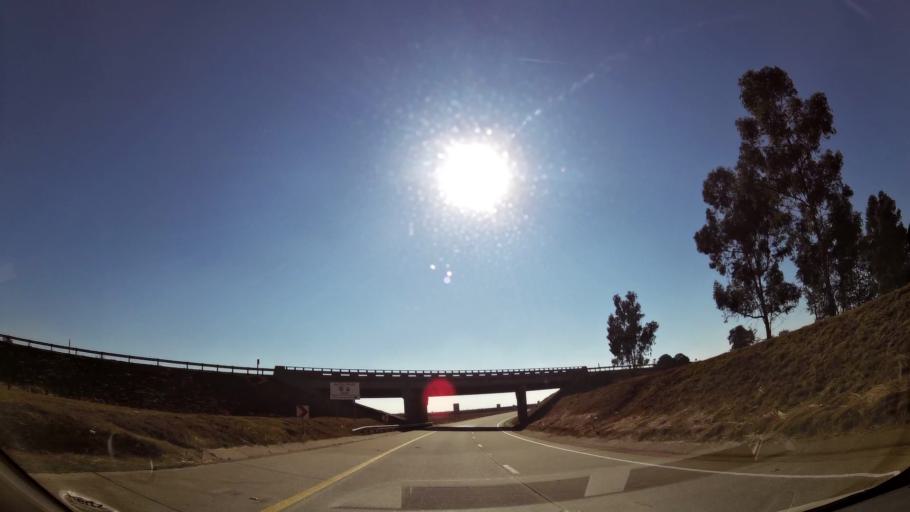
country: ZA
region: Mpumalanga
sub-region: Nkangala District Municipality
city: Witbank
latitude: -25.8969
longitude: 29.2541
